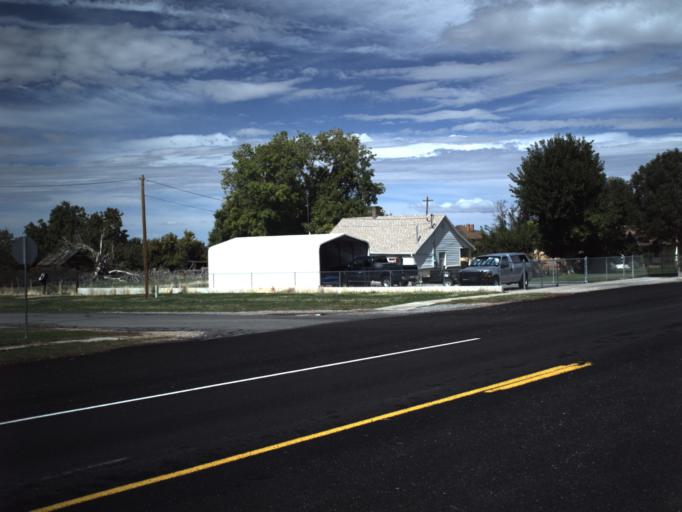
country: US
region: Utah
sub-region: Millard County
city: Fillmore
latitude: 38.7990
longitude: -112.4377
